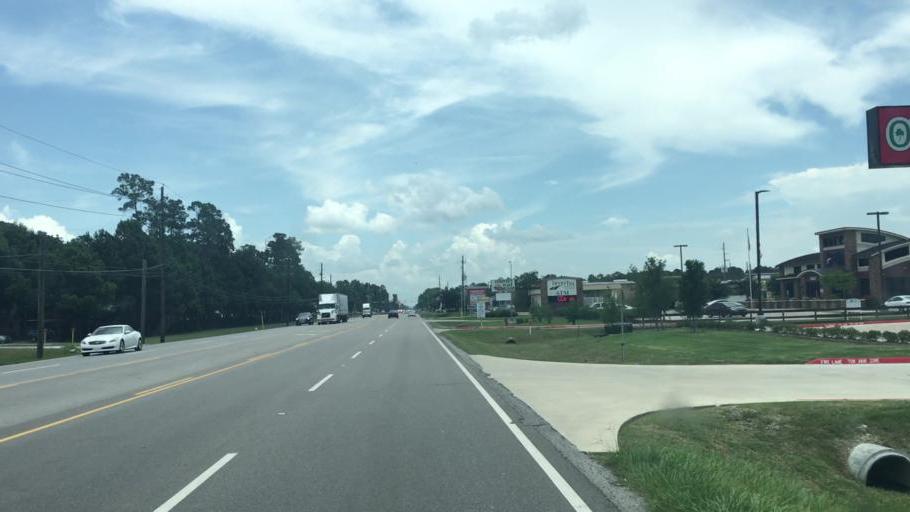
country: US
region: Texas
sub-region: Harris County
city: Atascocita
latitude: 29.9870
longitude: -95.1970
